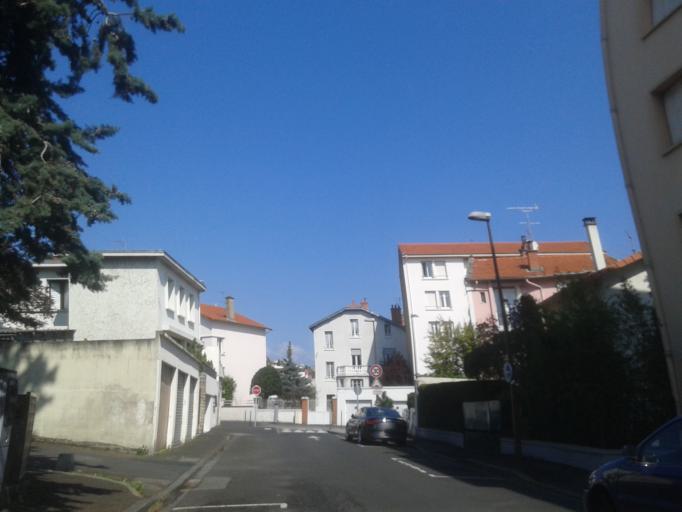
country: FR
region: Auvergne
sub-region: Departement du Puy-de-Dome
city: Chamalieres
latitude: 45.7774
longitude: 3.0637
